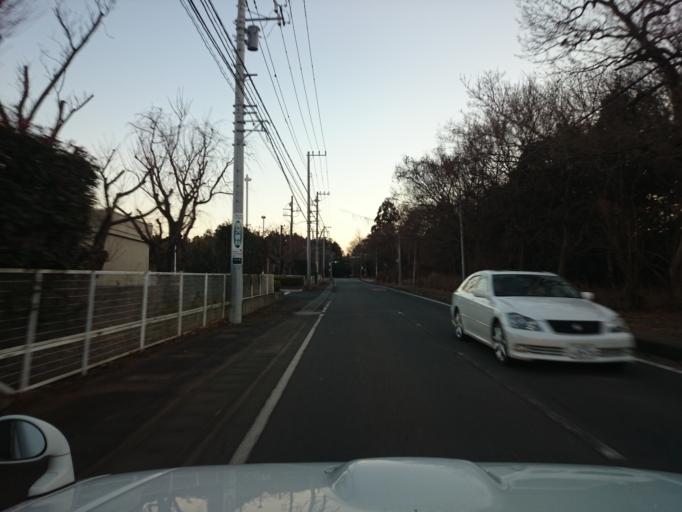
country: JP
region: Ibaraki
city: Ishige
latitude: 36.0798
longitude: 140.0483
